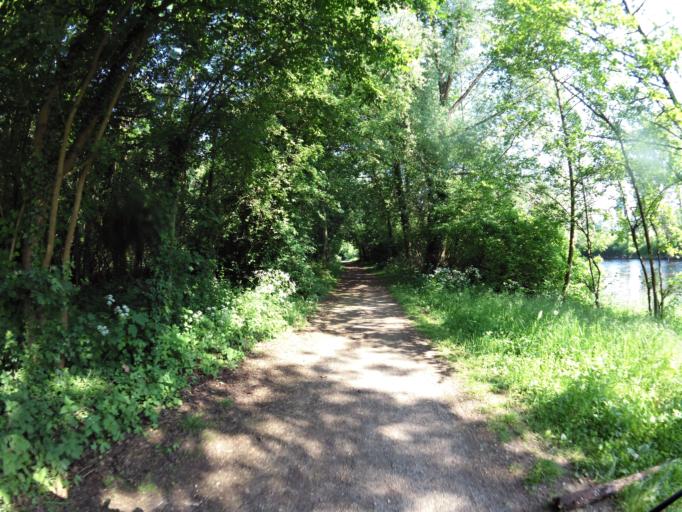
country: DE
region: North Rhine-Westphalia
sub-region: Regierungsbezirk Koln
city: Linnich
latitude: 50.9594
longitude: 6.2897
